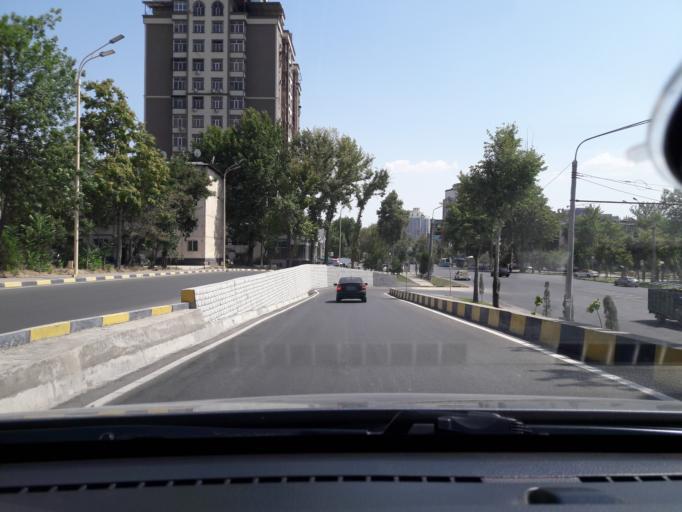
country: TJ
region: Dushanbe
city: Dushanbe
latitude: 38.5684
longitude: 68.7551
